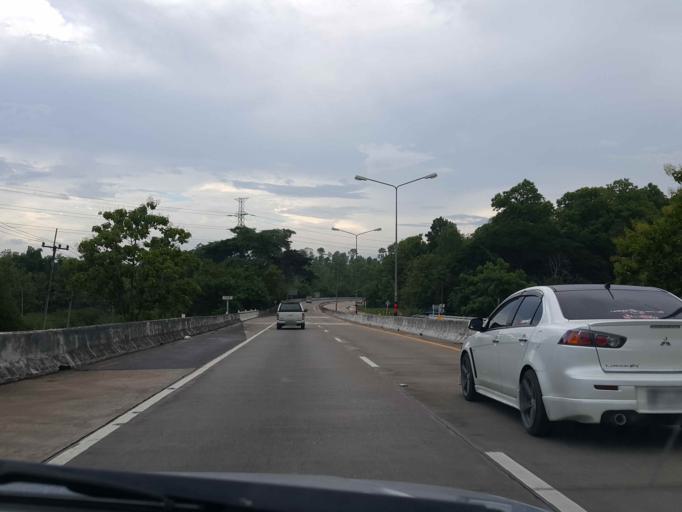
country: TH
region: Lampang
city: Hang Chat
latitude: 18.3266
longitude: 99.2801
